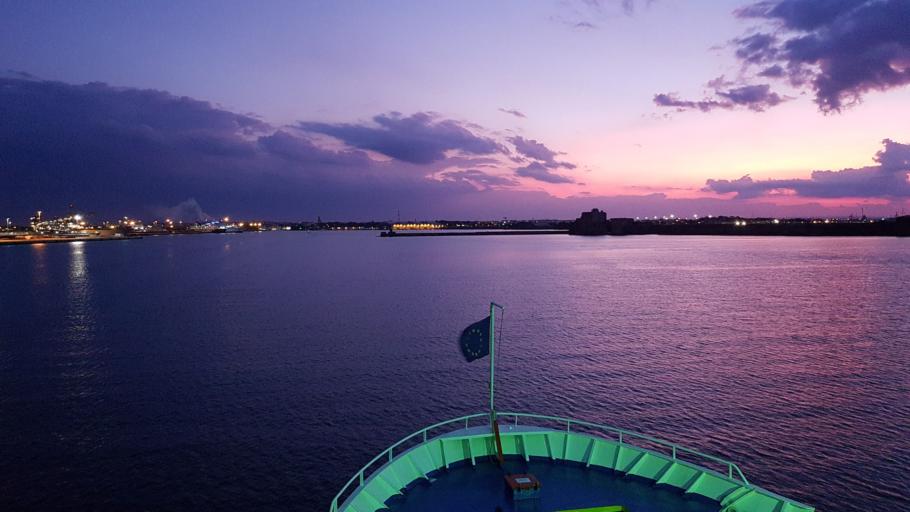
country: IT
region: Apulia
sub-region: Provincia di Brindisi
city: Materdomini
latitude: 40.6559
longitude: 17.9785
